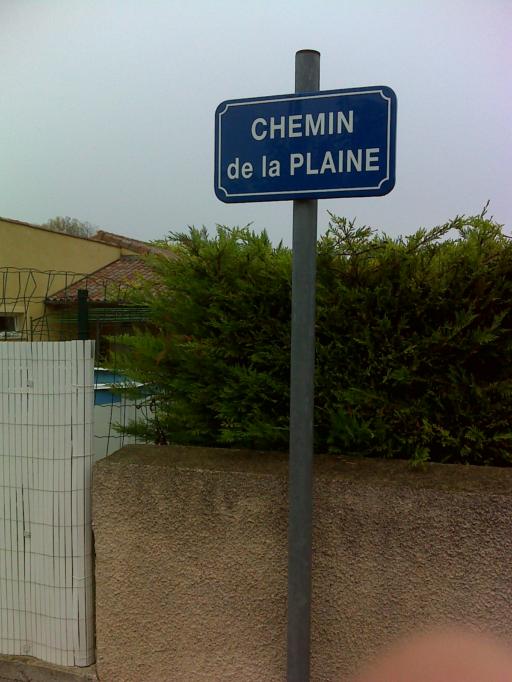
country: FR
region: Rhone-Alpes
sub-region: Departement de la Drome
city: La Roche-de-Glun
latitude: 45.0184
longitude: 4.8388
